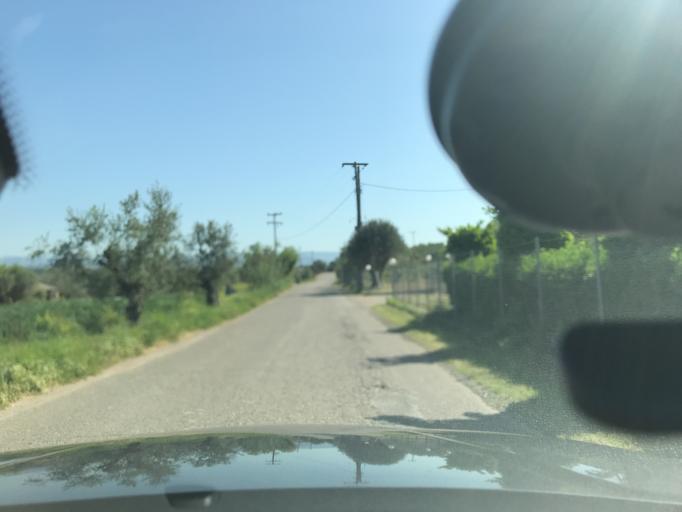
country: GR
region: West Greece
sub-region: Nomos Ileias
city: Epitalion
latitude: 37.6404
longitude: 21.5168
